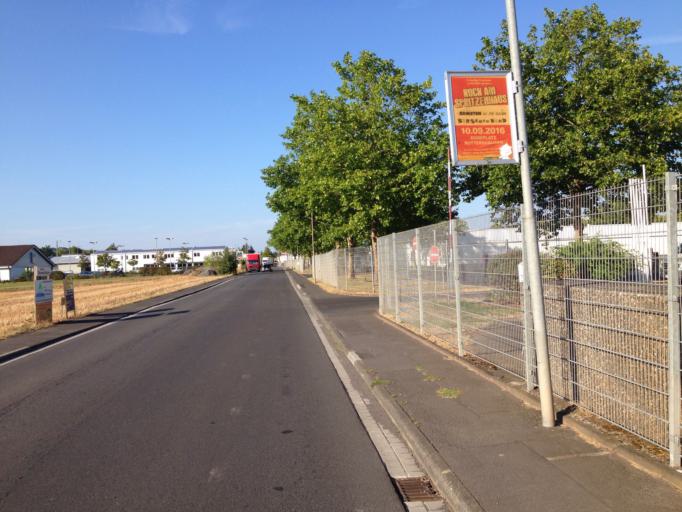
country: DE
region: Hesse
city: Lollar
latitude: 50.6386
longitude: 8.6982
